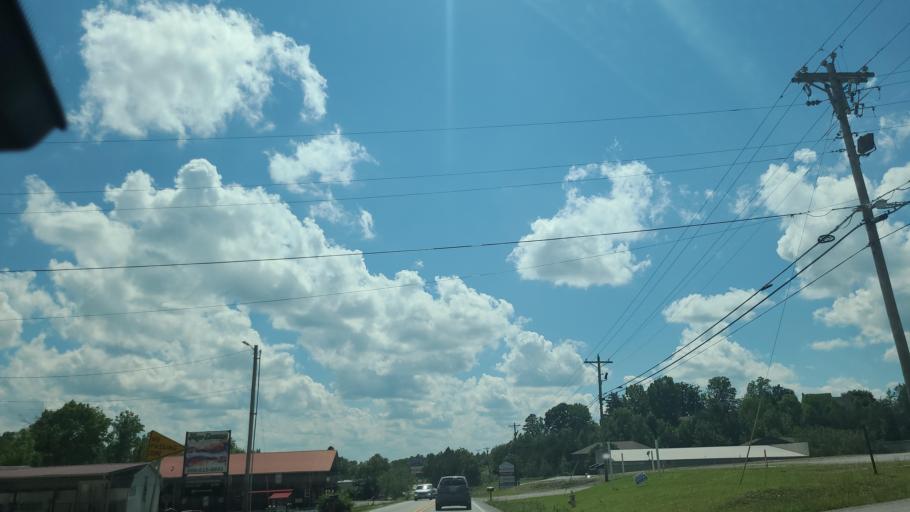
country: US
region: Kentucky
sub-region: Whitley County
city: Corbin
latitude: 36.9121
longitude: -84.1451
